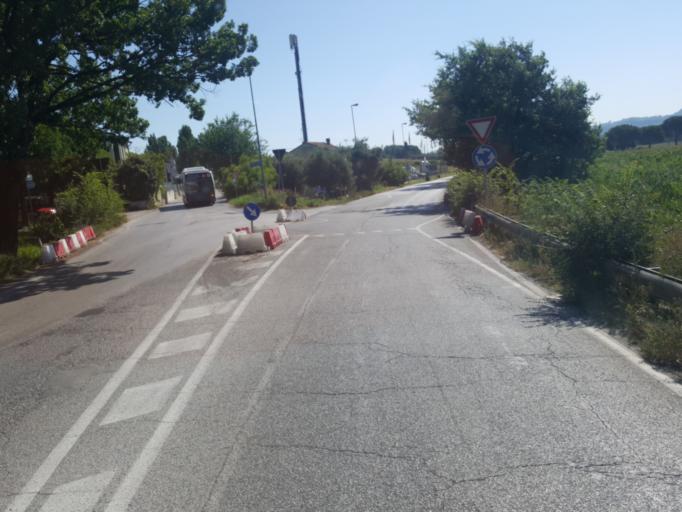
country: IT
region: The Marches
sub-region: Provincia di Pesaro e Urbino
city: Borgo Santa Maria
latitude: 43.8753
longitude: 12.8070
